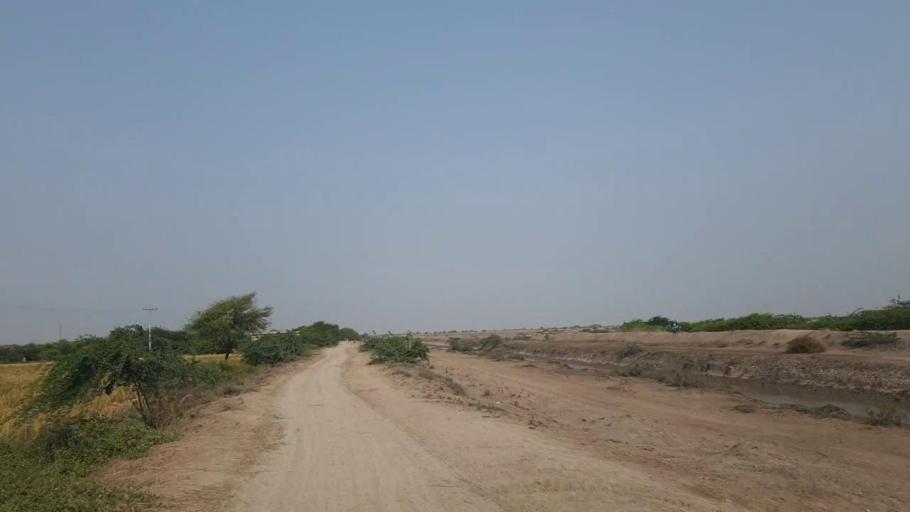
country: PK
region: Sindh
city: Badin
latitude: 24.7155
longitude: 68.7717
